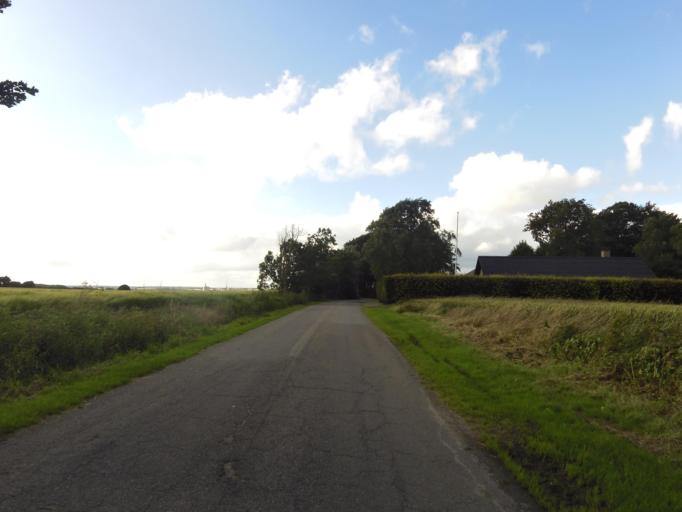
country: DK
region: South Denmark
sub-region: Tonder Kommune
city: Toftlund
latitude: 55.1501
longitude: 9.0856
